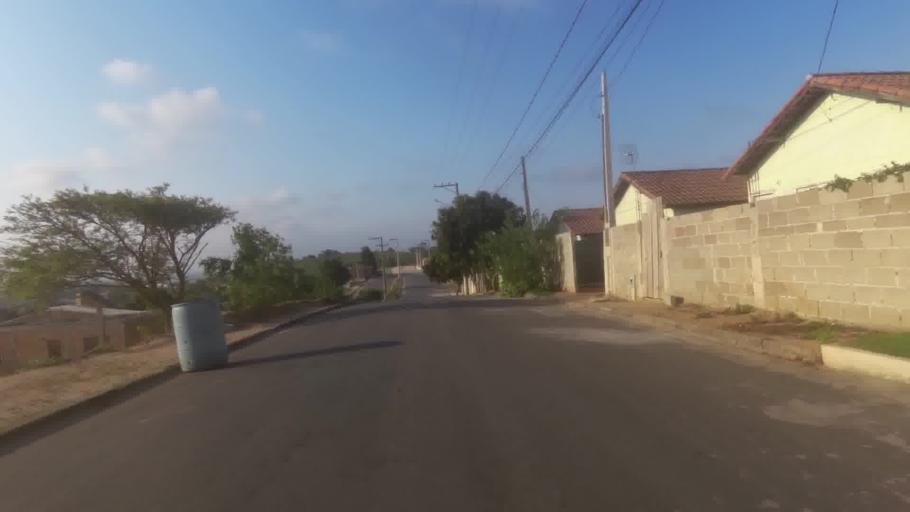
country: BR
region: Espirito Santo
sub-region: Itapemirim
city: Itapemirim
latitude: -21.0184
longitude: -40.8364
